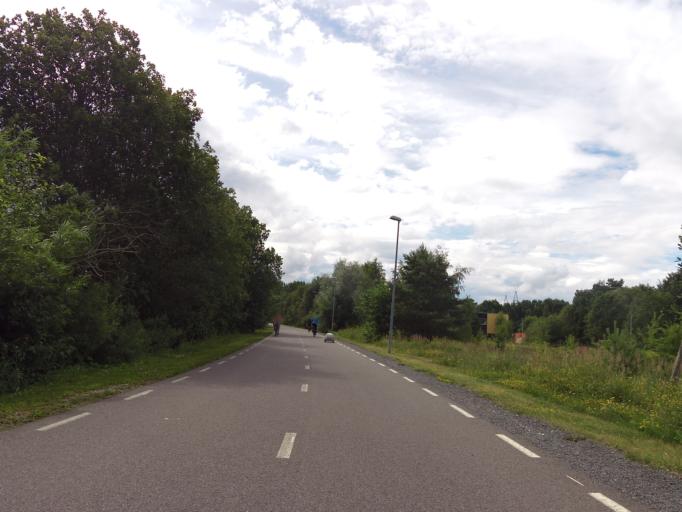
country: EE
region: Harju
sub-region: Saue vald
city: Laagri
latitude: 59.4043
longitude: 24.6442
